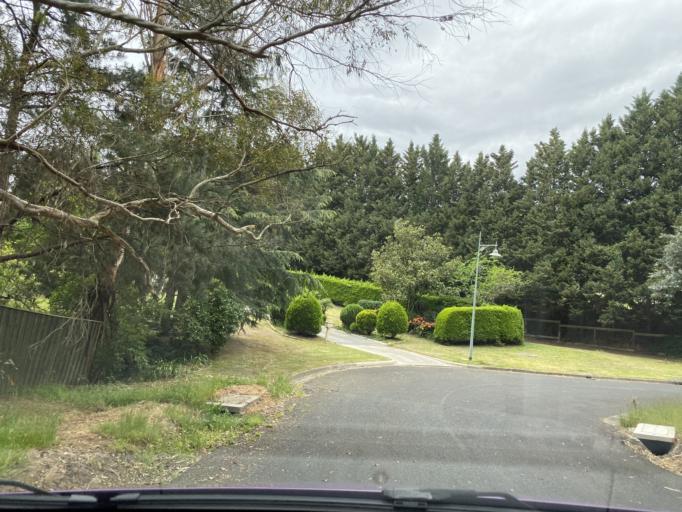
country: AU
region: Victoria
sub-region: Manningham
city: Templestowe Lower
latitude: -37.7635
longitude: 145.1302
